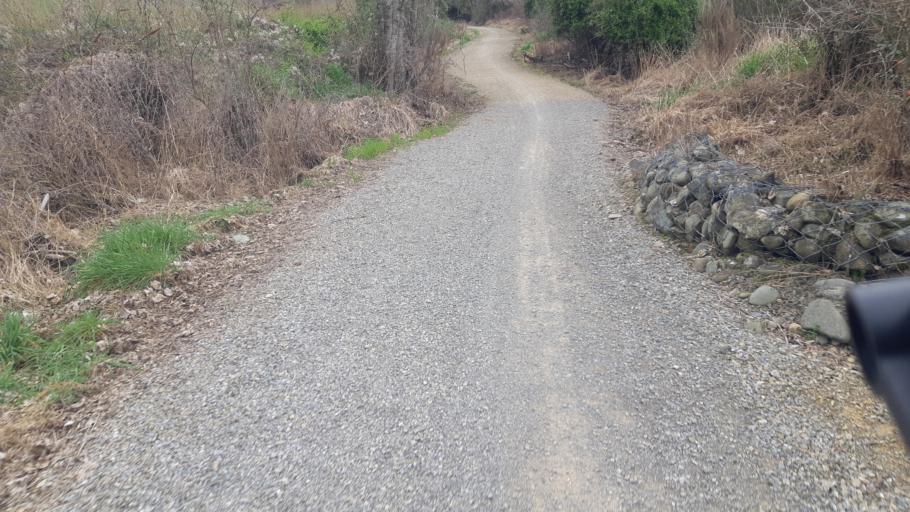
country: NZ
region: Tasman
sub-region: Tasman District
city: Wakefield
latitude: -41.4044
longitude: 173.0245
